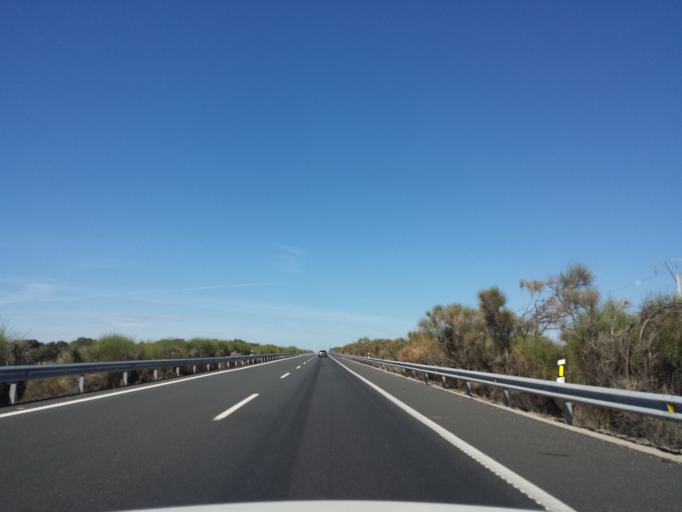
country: ES
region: Extremadura
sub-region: Provincia de Caceres
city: Peraleda de la Mata
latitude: 39.8902
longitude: -5.4405
